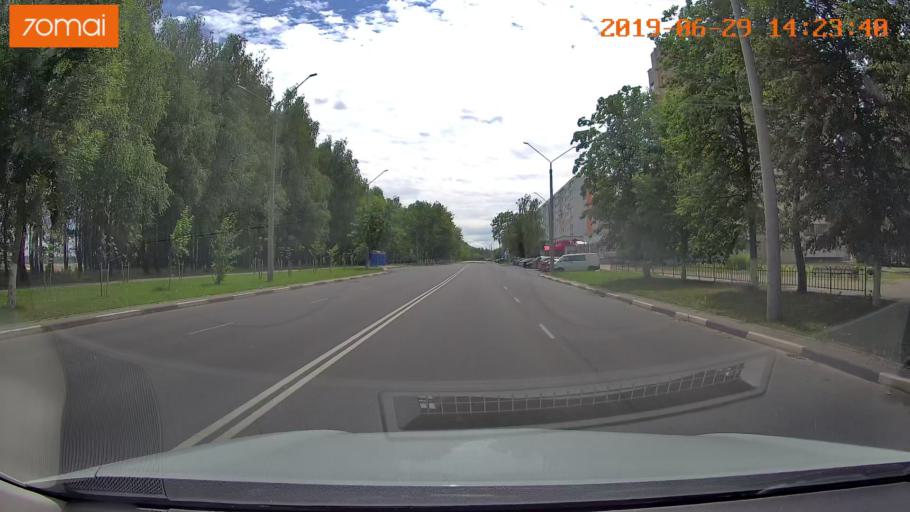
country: BY
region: Minsk
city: Salihorsk
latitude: 52.7846
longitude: 27.5533
